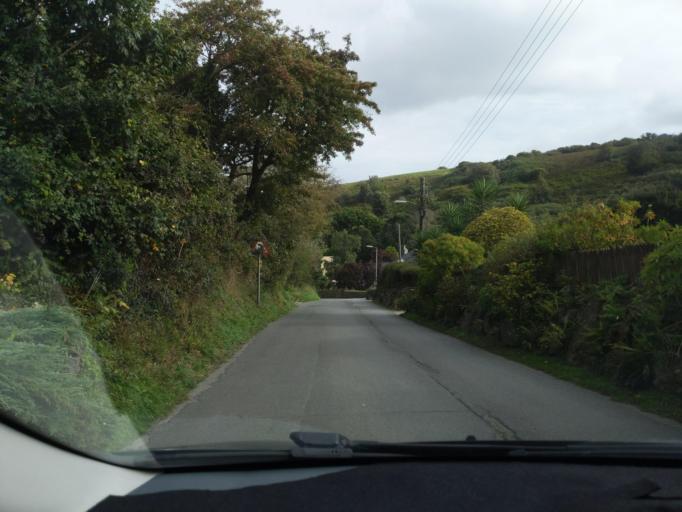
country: GB
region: England
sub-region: Cornwall
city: Mevagissey
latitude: 50.2395
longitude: -4.7956
